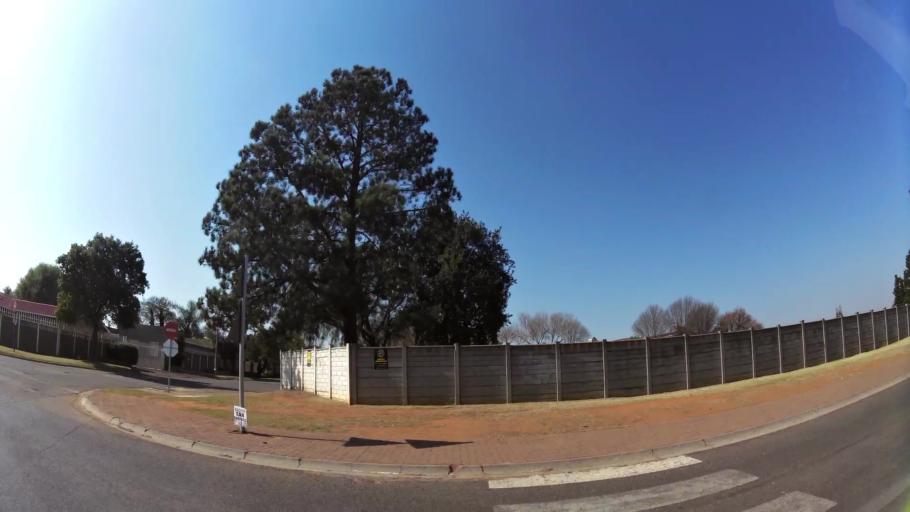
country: ZA
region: Gauteng
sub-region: Ekurhuleni Metropolitan Municipality
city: Boksburg
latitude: -26.2484
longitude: 28.2756
